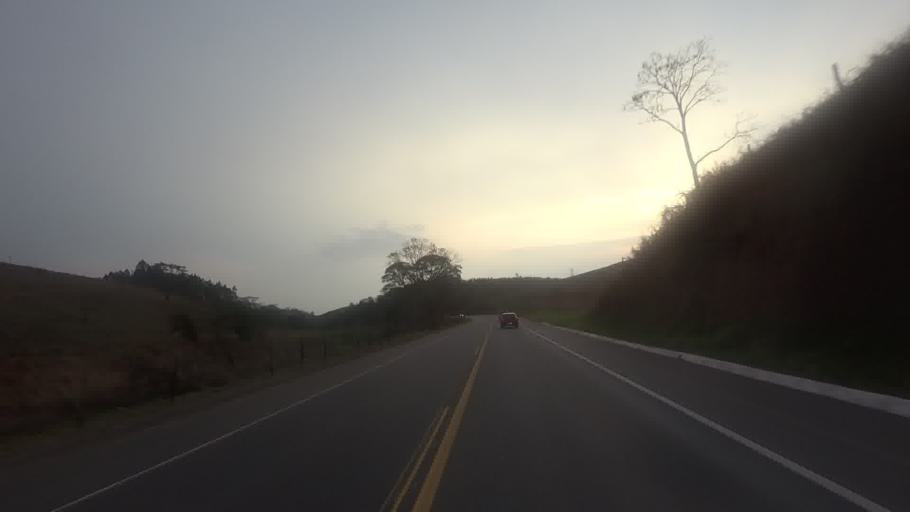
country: BR
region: Rio de Janeiro
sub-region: Carmo
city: Carmo
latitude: -21.7797
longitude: -42.5404
